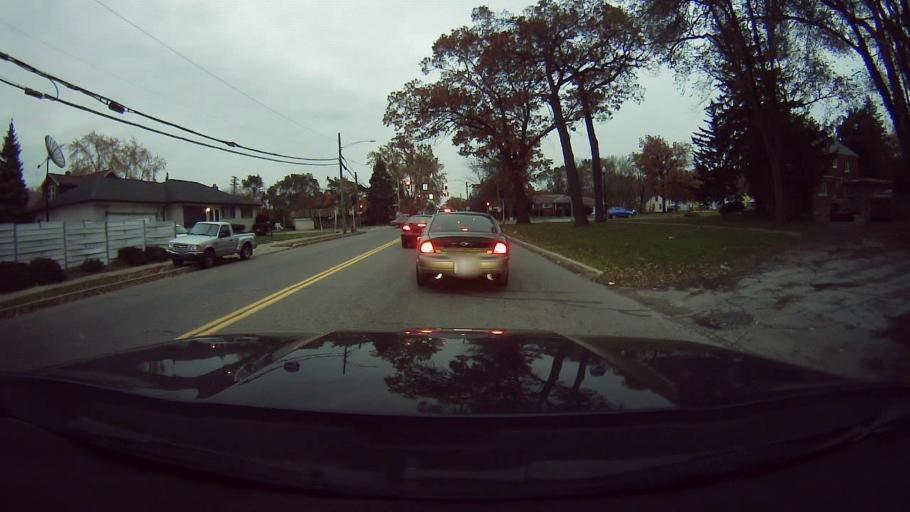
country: US
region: Michigan
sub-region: Oakland County
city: Hazel Park
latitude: 42.4411
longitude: -83.0636
